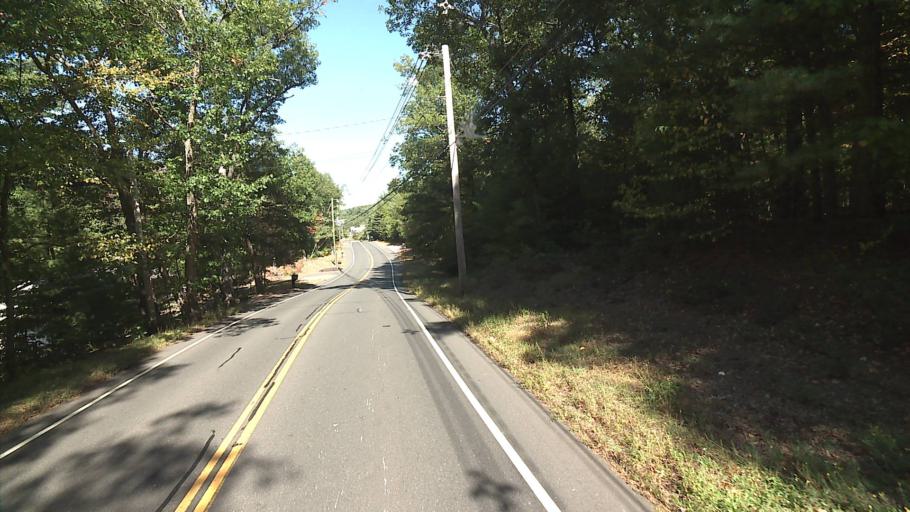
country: US
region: Connecticut
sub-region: Hartford County
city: Manchester
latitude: 41.7092
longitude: -72.5280
